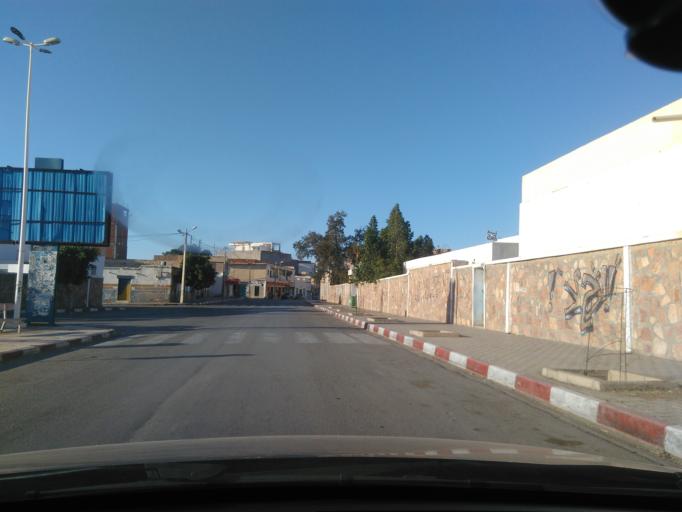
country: TN
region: Tataouine
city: Tataouine
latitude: 32.9295
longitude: 10.4493
